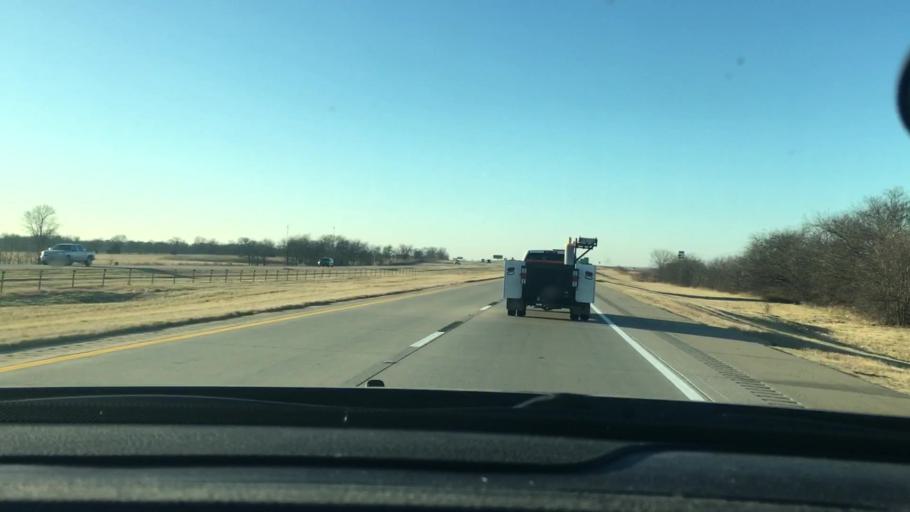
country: US
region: Oklahoma
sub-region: Murray County
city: Davis
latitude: 34.3409
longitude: -97.1492
